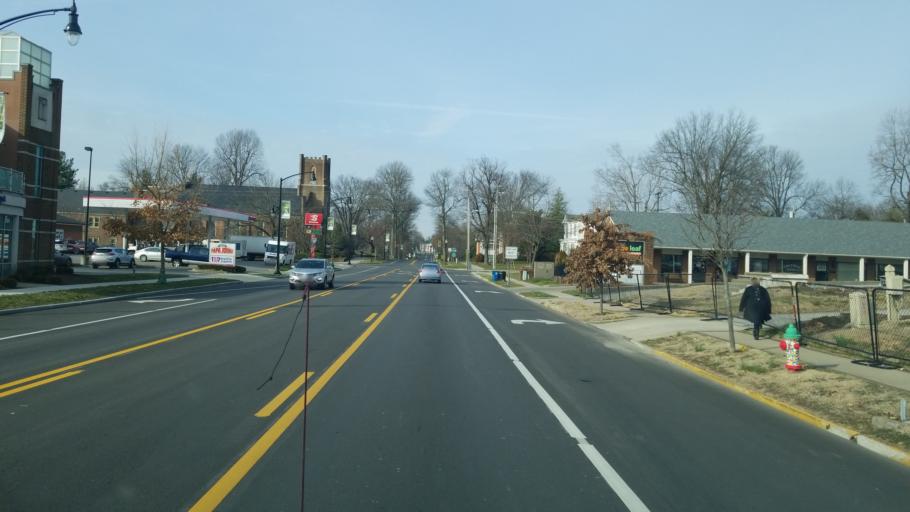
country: US
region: Kentucky
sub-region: Boyle County
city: Danville
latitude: 37.6461
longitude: -84.7759
